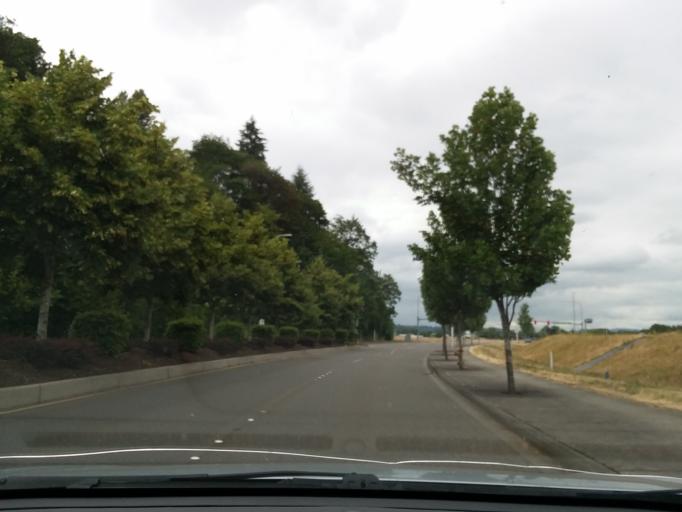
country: US
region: Washington
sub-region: King County
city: SeaTac
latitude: 47.4364
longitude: -122.2642
